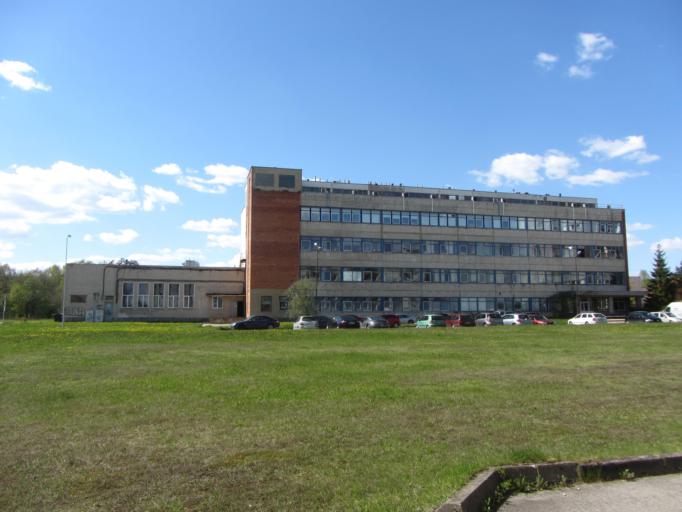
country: LT
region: Vilnius County
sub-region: Vilnius
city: Fabijoniskes
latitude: 54.7515
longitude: 25.2620
